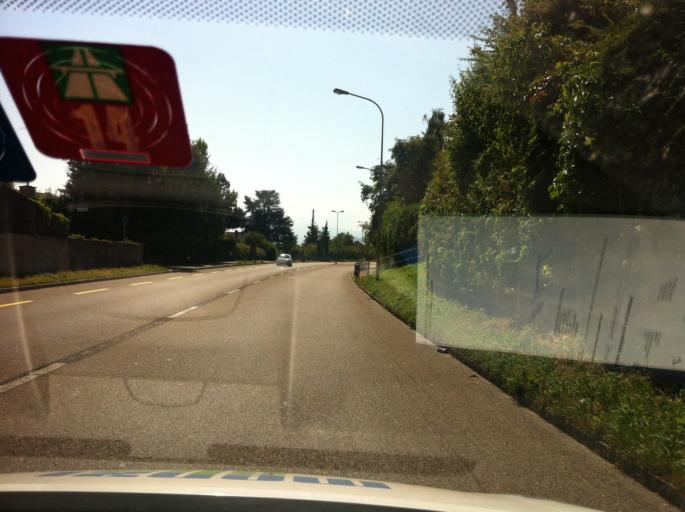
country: CH
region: Zurich
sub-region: Bezirk Horgen
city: Thalwil / Nord
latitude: 47.2984
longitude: 8.5529
